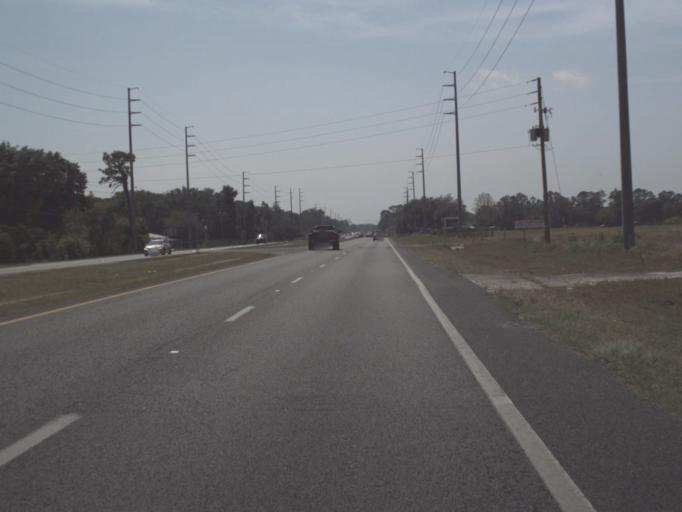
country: US
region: Florida
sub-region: Lake County
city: Eustis
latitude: 28.8881
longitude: -81.6870
